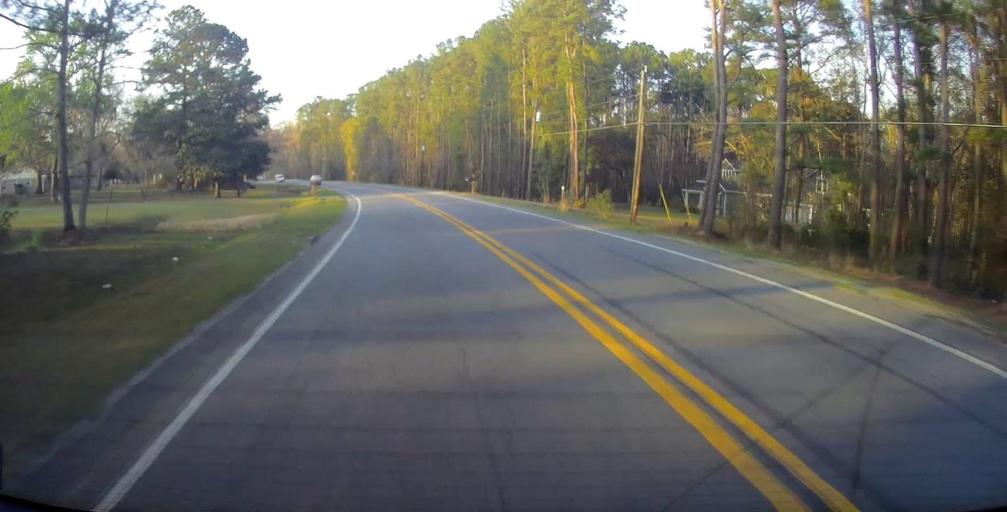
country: US
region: Georgia
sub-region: Chatham County
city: Bloomingdale
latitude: 32.1645
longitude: -81.3849
